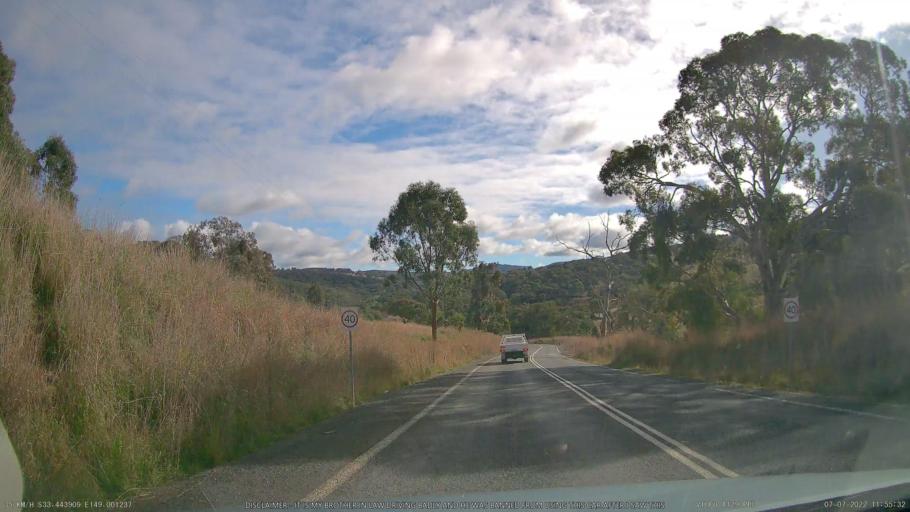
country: AU
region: New South Wales
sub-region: Blayney
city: Millthorpe
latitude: -33.4437
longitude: 149.0011
